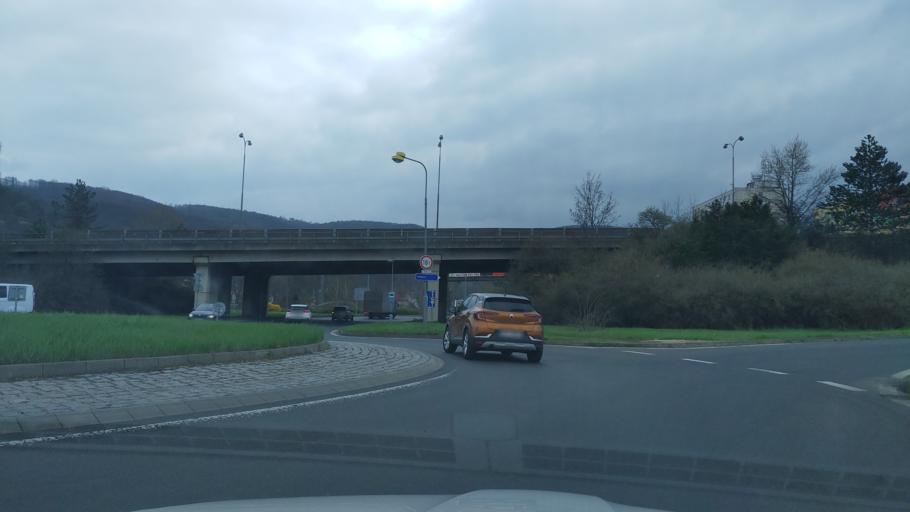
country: CZ
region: Ustecky
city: Trmice
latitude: 50.6486
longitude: 14.0053
